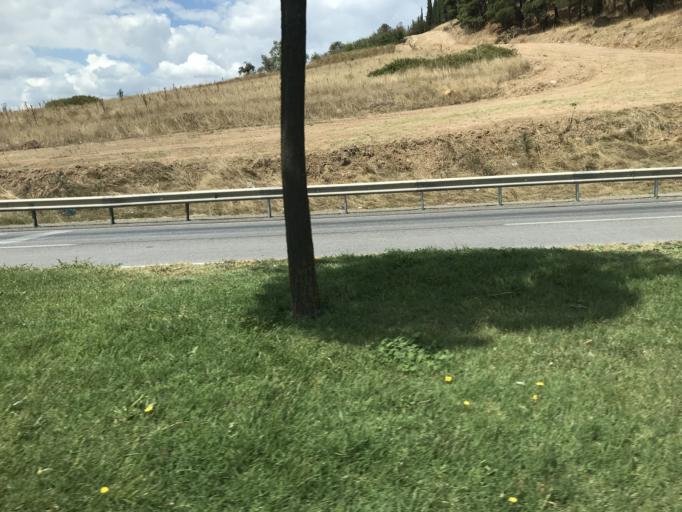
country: TR
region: Balikesir
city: Balikesir
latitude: 39.6957
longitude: 27.9641
